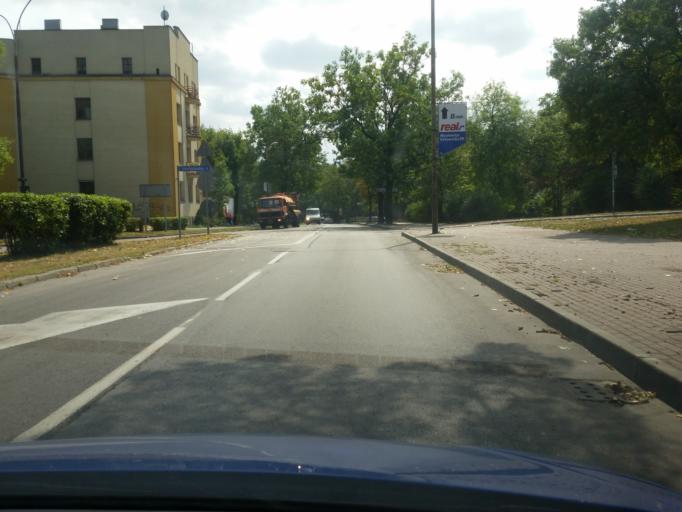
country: PL
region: Silesian Voivodeship
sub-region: Sosnowiec
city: Sosnowiec
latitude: 50.2726
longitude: 19.1344
